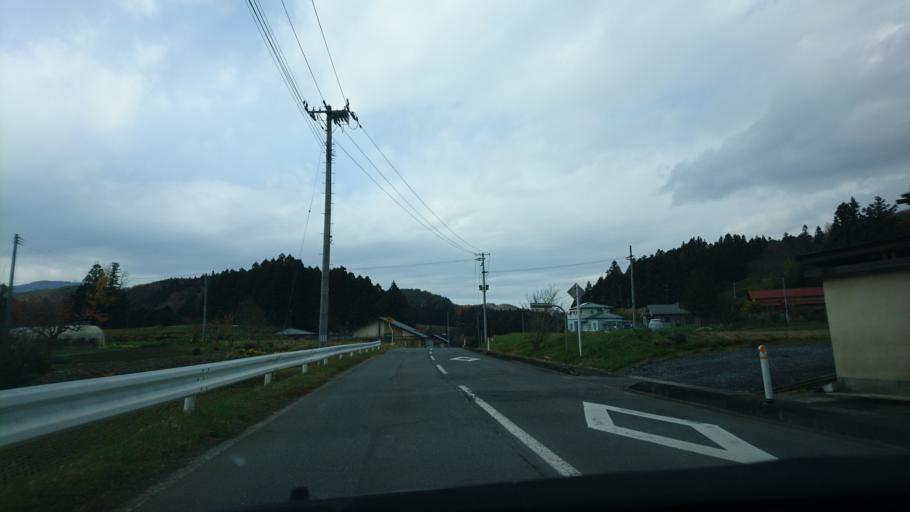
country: JP
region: Iwate
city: Ichinoseki
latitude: 38.9955
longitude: 141.2472
